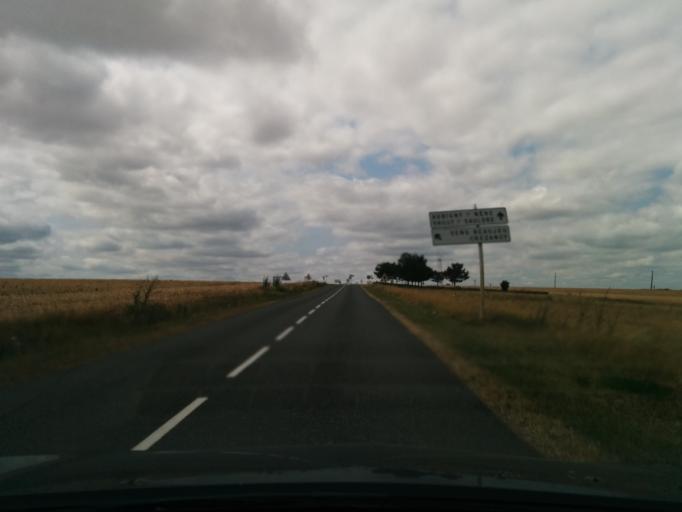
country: FR
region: Centre
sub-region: Departement du Cher
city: Sancerre
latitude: 47.3231
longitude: 2.7917
